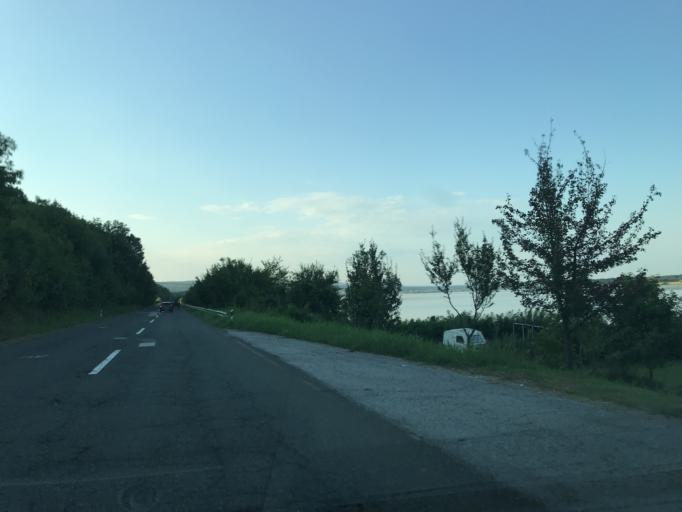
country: RO
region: Mehedinti
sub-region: Comuna Gogosu
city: Ostrovu Mare
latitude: 44.4586
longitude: 22.4518
